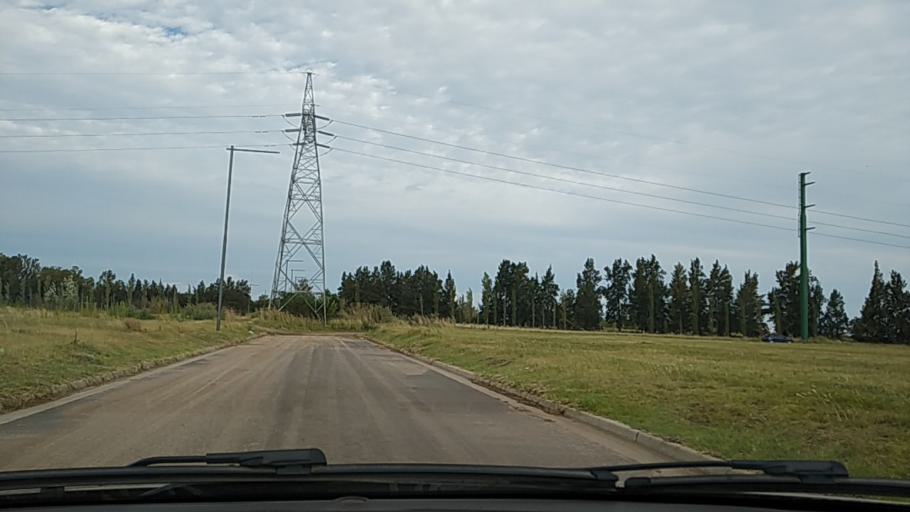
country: AR
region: Santa Fe
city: Perez
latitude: -32.9466
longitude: -60.7648
